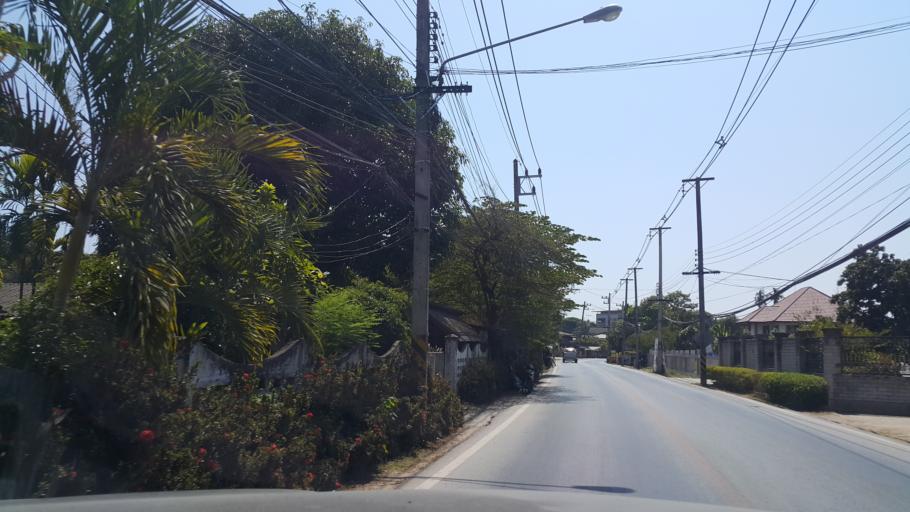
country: TH
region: Chiang Mai
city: San Sai
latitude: 18.8572
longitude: 99.0498
